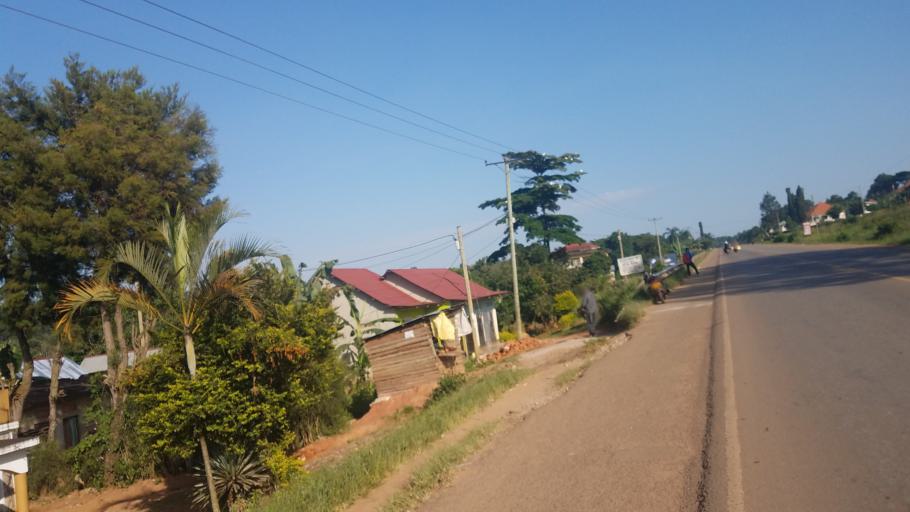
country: UG
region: Central Region
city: Masaka
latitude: -0.3391
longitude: 31.7028
